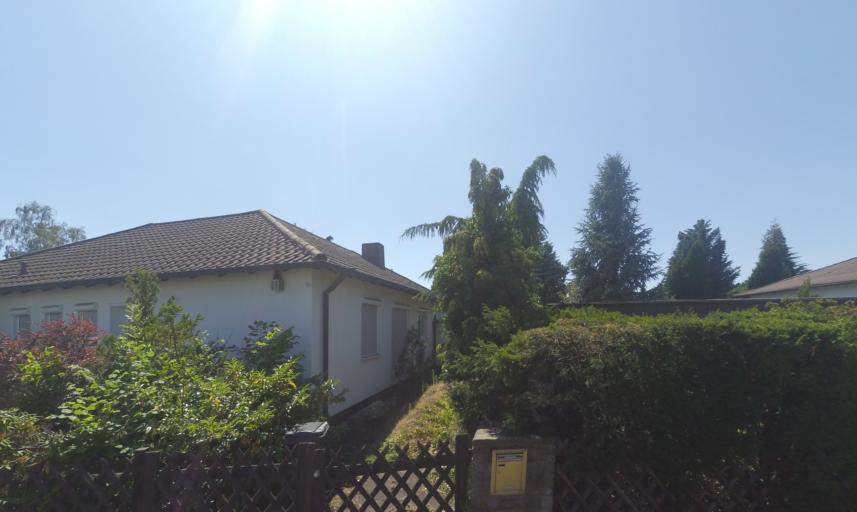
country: DE
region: Rheinland-Pfalz
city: Limburgerhof
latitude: 49.4182
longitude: 8.4008
